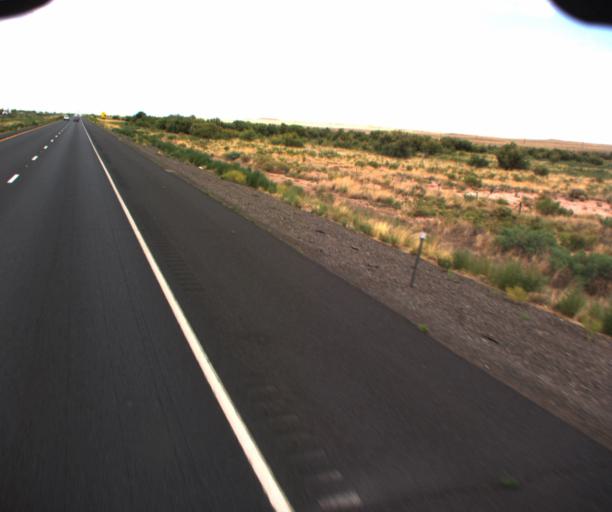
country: US
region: Arizona
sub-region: Navajo County
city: Winslow
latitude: 34.9868
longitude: -110.5592
